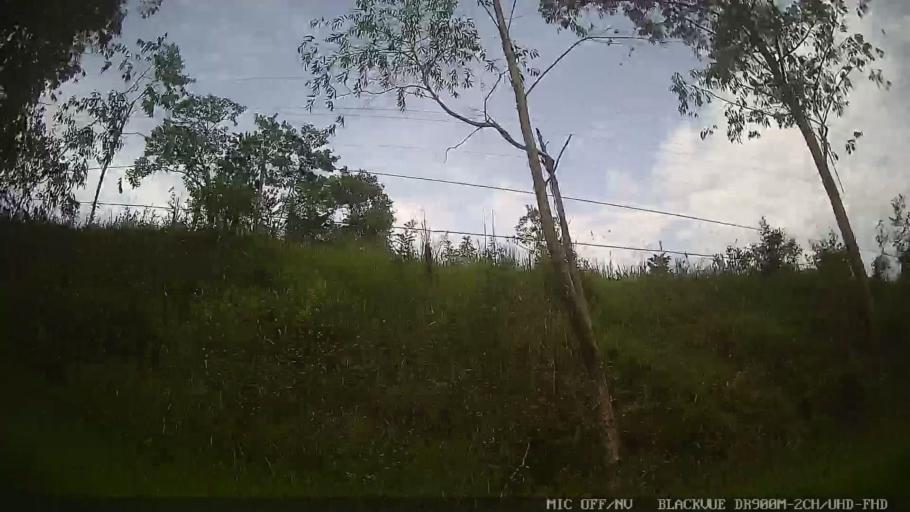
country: BR
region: Sao Paulo
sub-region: Suzano
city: Suzano
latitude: -23.6754
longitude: -46.2514
